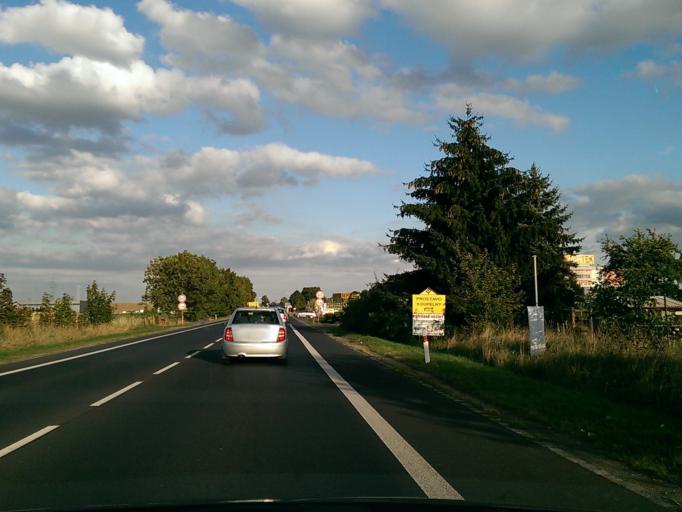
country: CZ
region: Central Bohemia
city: Kosmonosy
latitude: 50.4090
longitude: 14.9505
